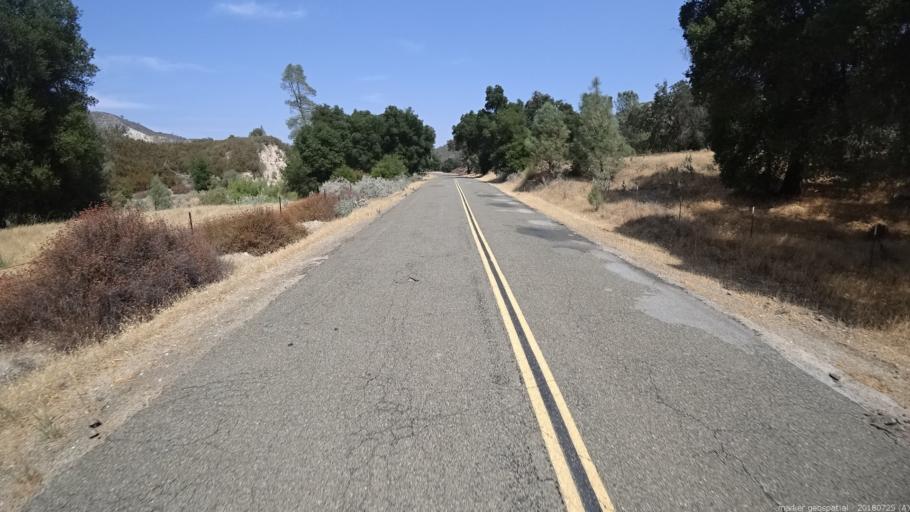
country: US
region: California
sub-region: San Luis Obispo County
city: San Miguel
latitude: 35.9017
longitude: -120.5518
